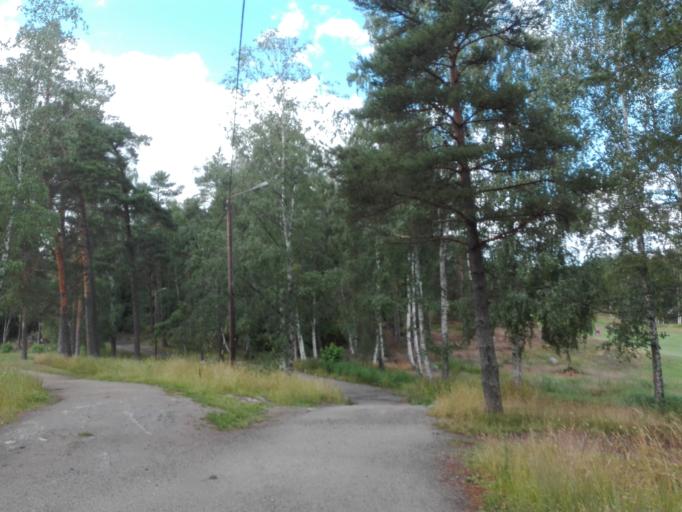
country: SE
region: Stockholm
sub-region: Nacka Kommun
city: Fisksatra
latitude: 59.2840
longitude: 18.2646
